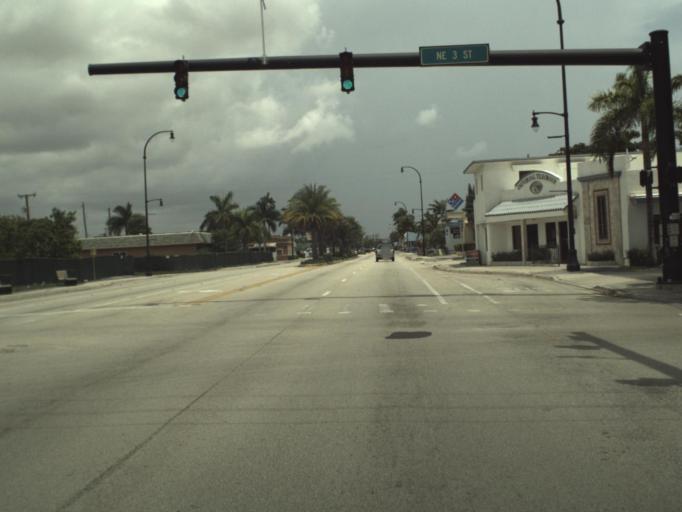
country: US
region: Florida
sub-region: Broward County
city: Hallandale Beach
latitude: 25.9892
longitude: -80.1424
